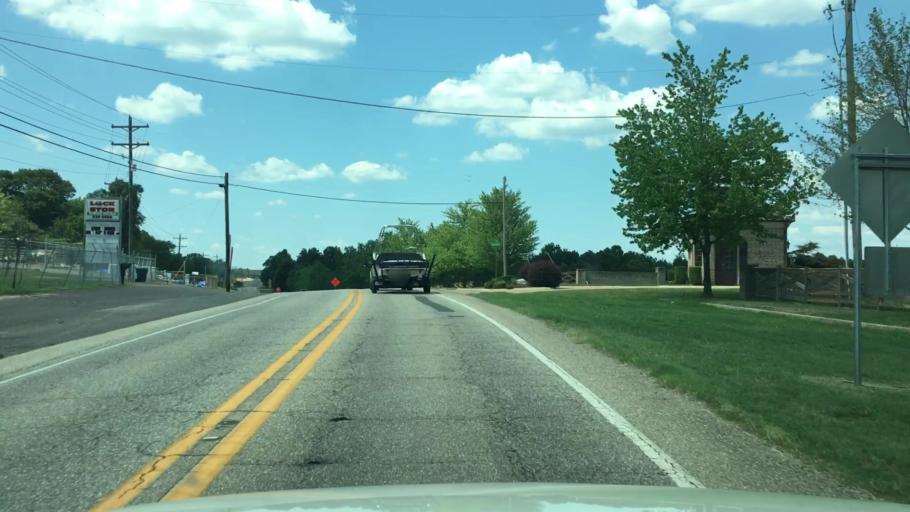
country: US
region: Arkansas
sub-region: Garland County
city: Lake Hamilton
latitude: 34.4070
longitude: -93.0912
